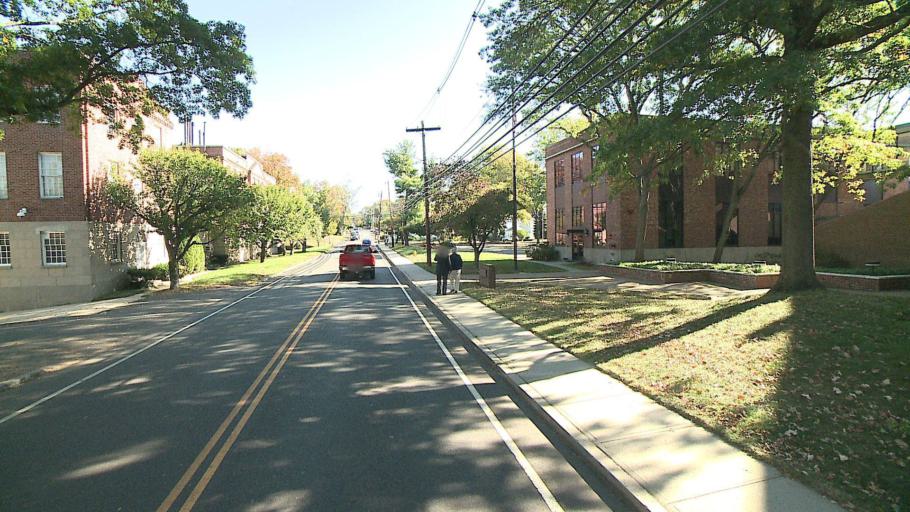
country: US
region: Connecticut
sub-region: Fairfield County
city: East Norwalk
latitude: 41.1043
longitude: -73.4018
